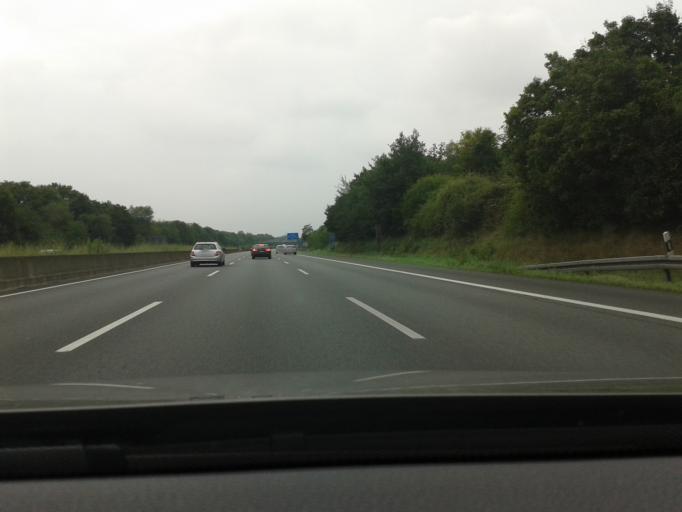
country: DE
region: Lower Saxony
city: Langenhagen
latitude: 52.4295
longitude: 9.7871
